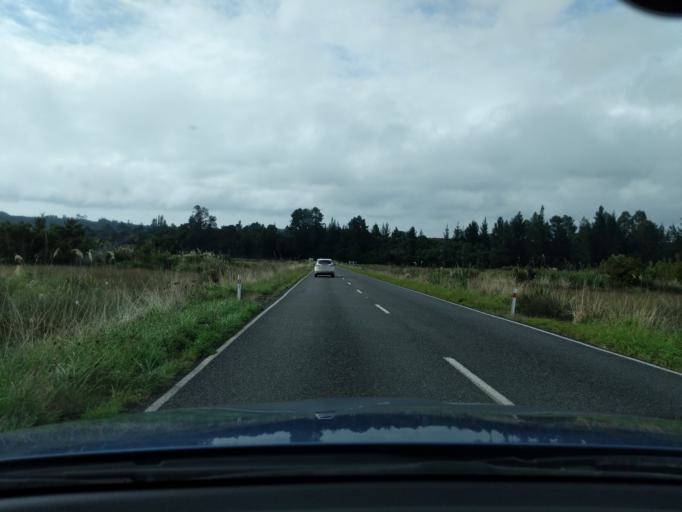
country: NZ
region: Tasman
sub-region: Tasman District
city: Takaka
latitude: -40.6794
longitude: 172.6647
